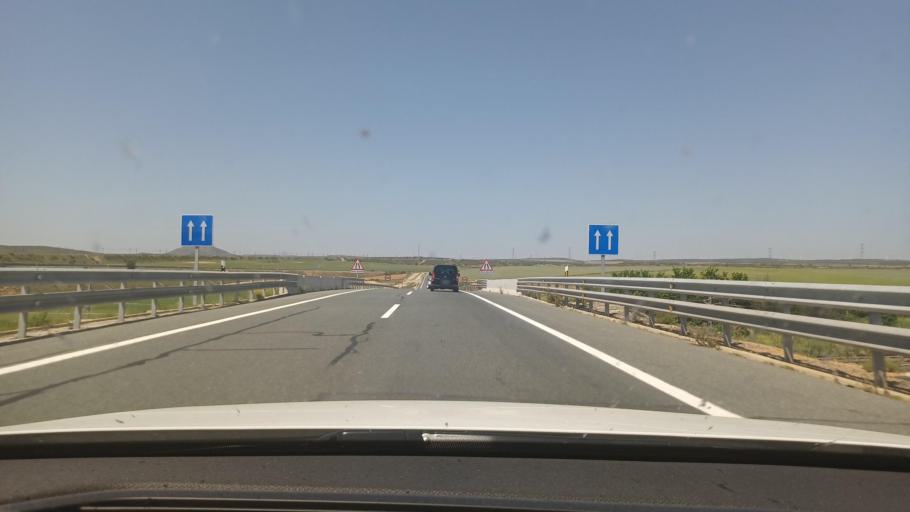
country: ES
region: Castille-La Mancha
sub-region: Provincia de Albacete
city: Alpera
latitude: 38.8786
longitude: -1.2270
